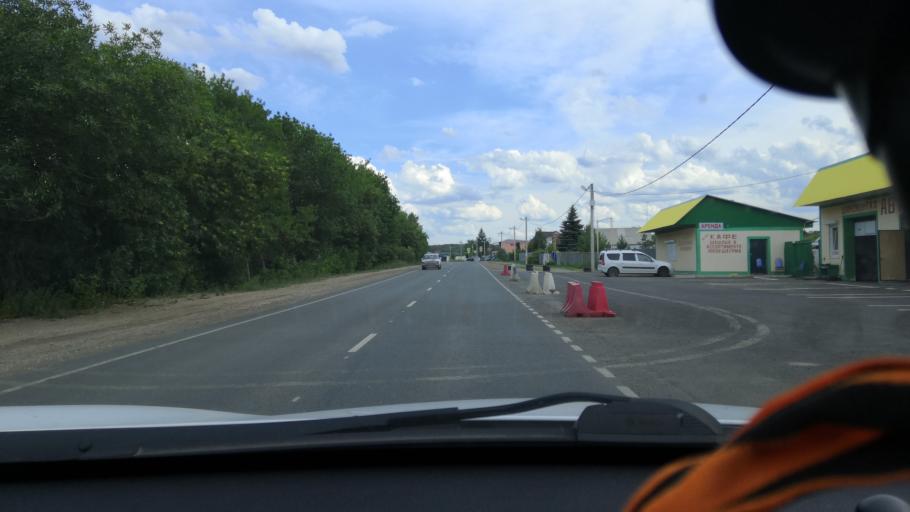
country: RU
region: Samara
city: Novosemeykino
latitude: 53.3810
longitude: 50.3352
